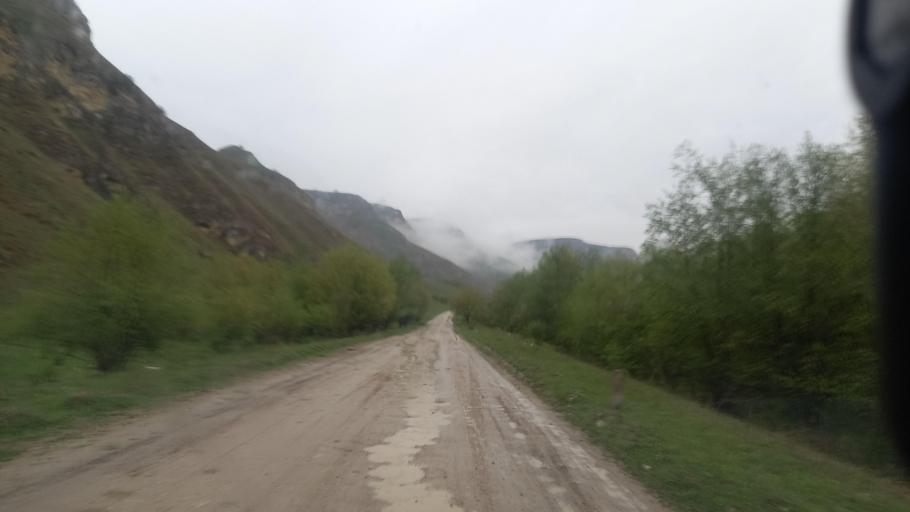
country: RU
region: Kabardino-Balkariya
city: Gundelen
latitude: 43.5982
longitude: 43.0603
